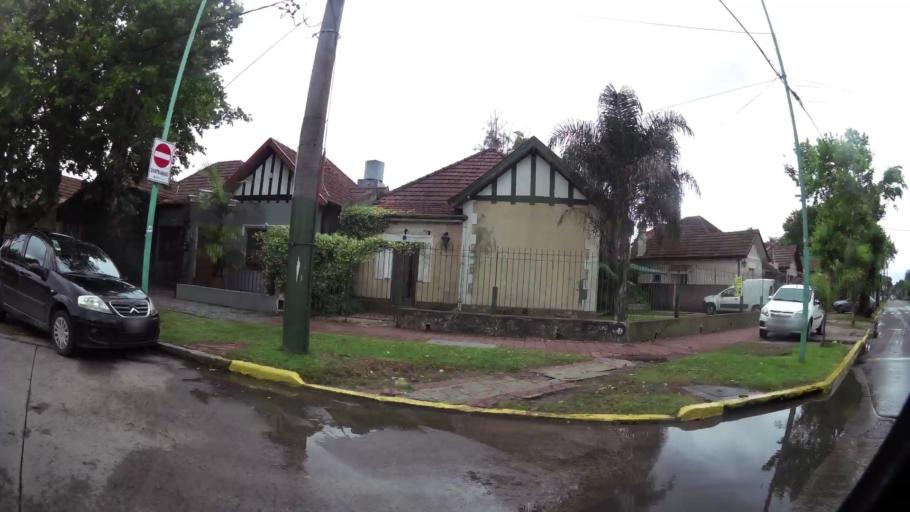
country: AR
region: Buenos Aires
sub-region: Partido de Lomas de Zamora
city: Lomas de Zamora
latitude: -34.7642
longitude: -58.3920
